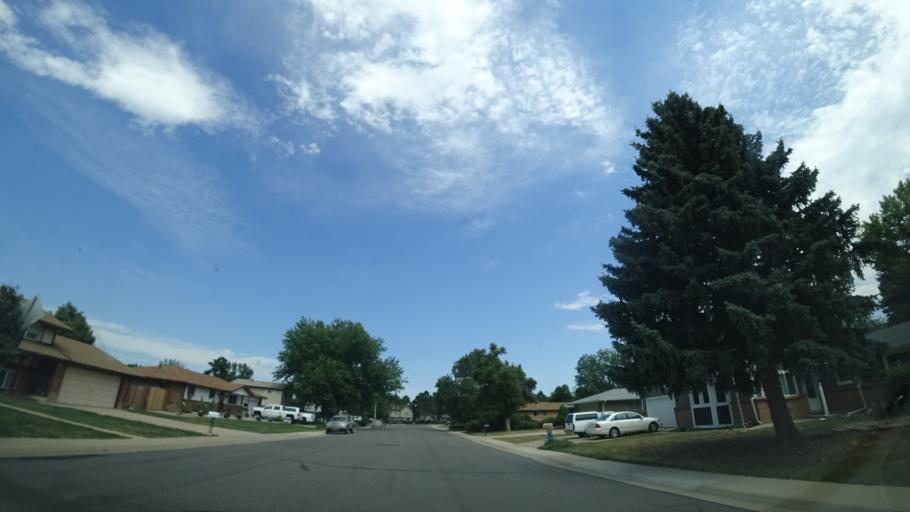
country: US
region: Colorado
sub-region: Jefferson County
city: Lakewood
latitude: 39.6934
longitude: -105.1023
